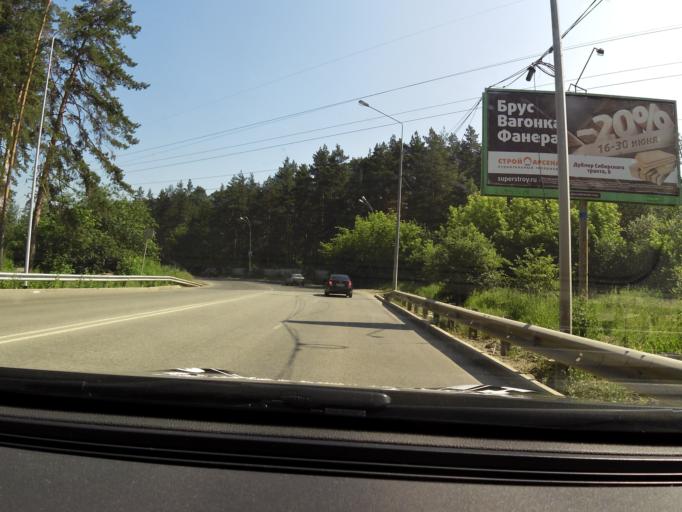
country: RU
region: Sverdlovsk
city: Shirokaya Rechka
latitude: 56.8132
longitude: 60.5186
